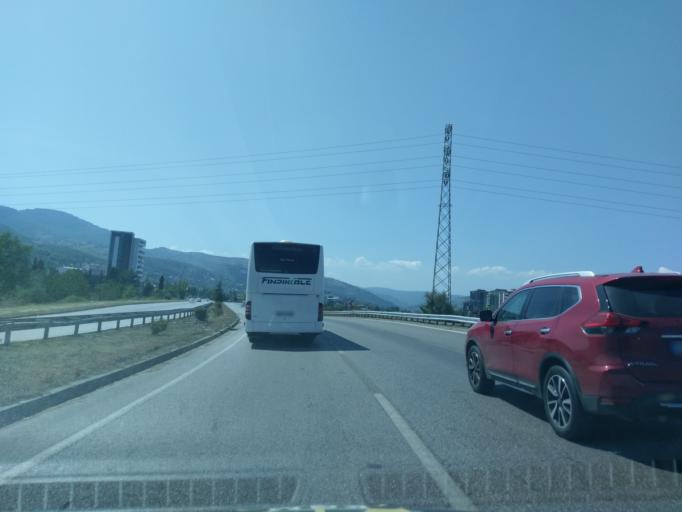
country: TR
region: Samsun
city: Samsun
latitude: 41.2593
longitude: 36.3316
